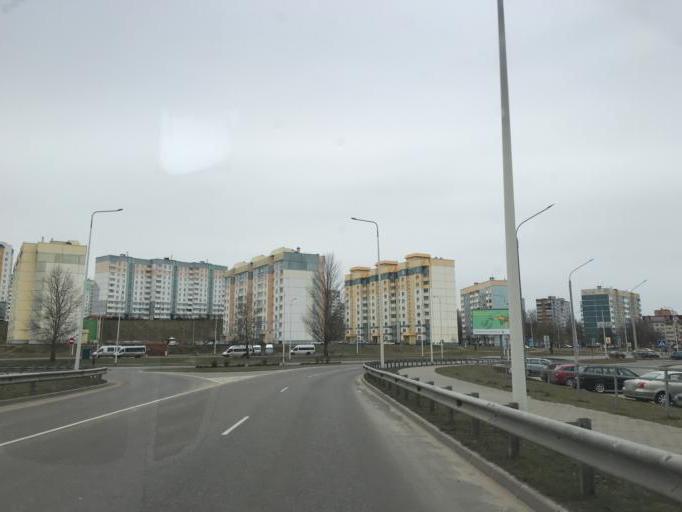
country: BY
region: Mogilev
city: Mahilyow
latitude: 53.8829
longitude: 30.3790
